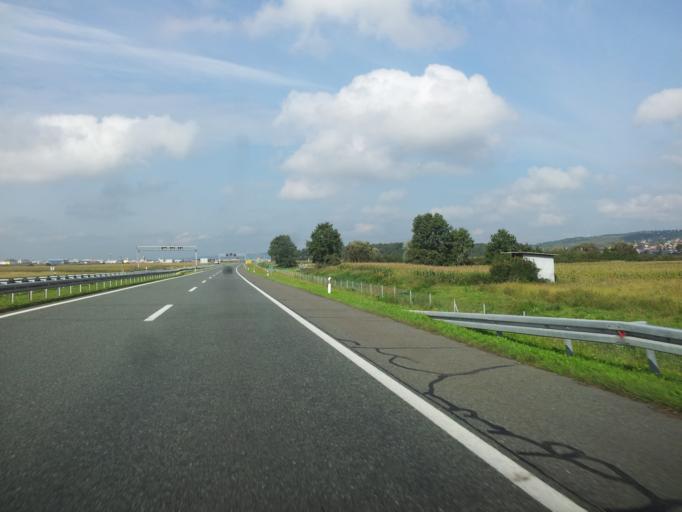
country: HR
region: Brodsko-Posavska
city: Bukovlje
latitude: 45.1753
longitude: 18.0880
